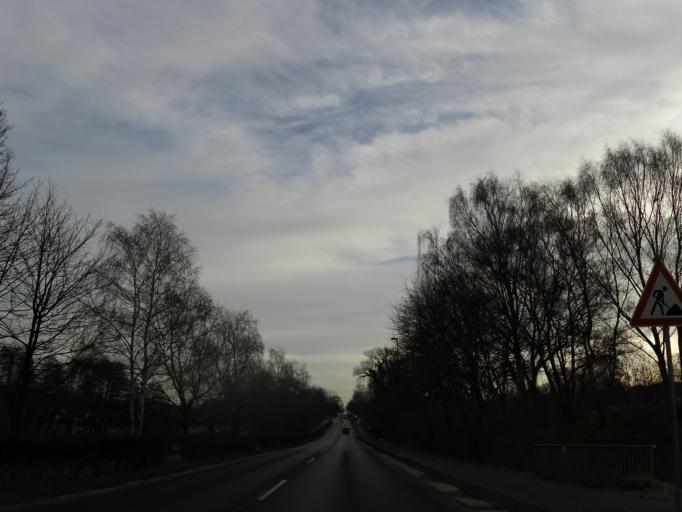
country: NL
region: Limburg
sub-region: Gemeente Vaals
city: Vaals
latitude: 50.7696
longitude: 6.0314
